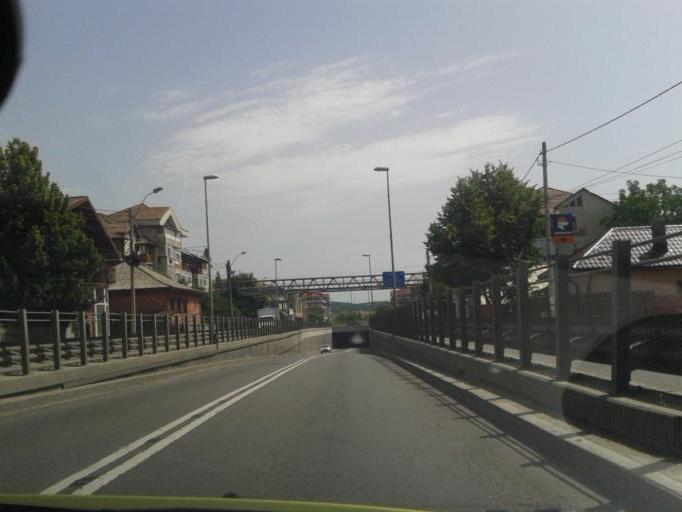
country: RO
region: Arges
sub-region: Comuna Bascov
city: Bascov
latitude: 44.8897
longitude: 24.8191
